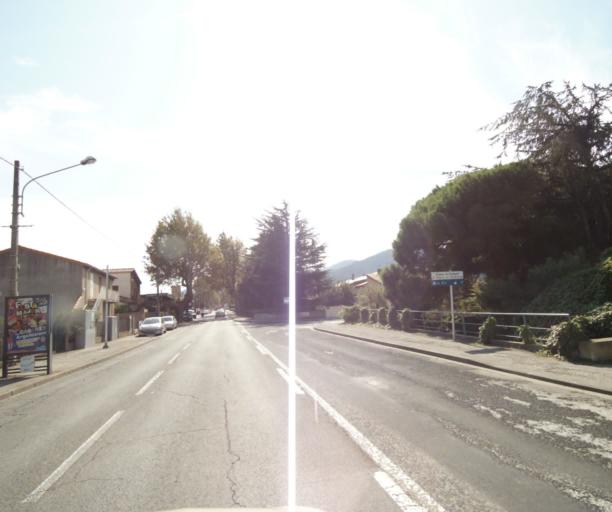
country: FR
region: Languedoc-Roussillon
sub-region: Departement des Pyrenees-Orientales
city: Argelers
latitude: 42.5497
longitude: 3.0187
